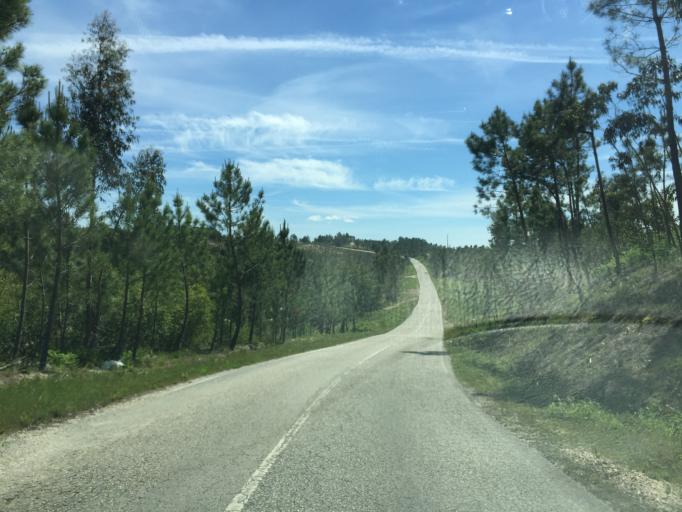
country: PT
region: Leiria
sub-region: Pombal
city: Lourical
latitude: 40.0640
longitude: -8.6992
